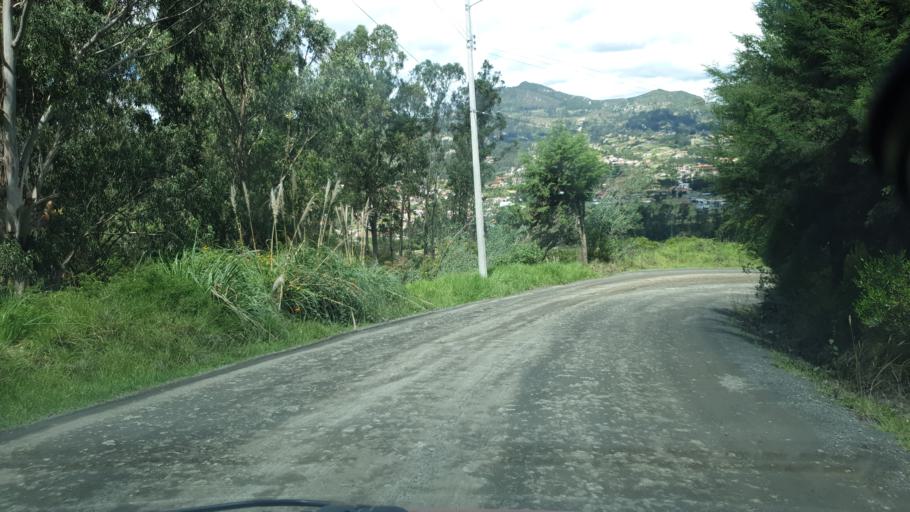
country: EC
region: Azuay
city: Llacao
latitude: -2.8401
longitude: -78.9026
